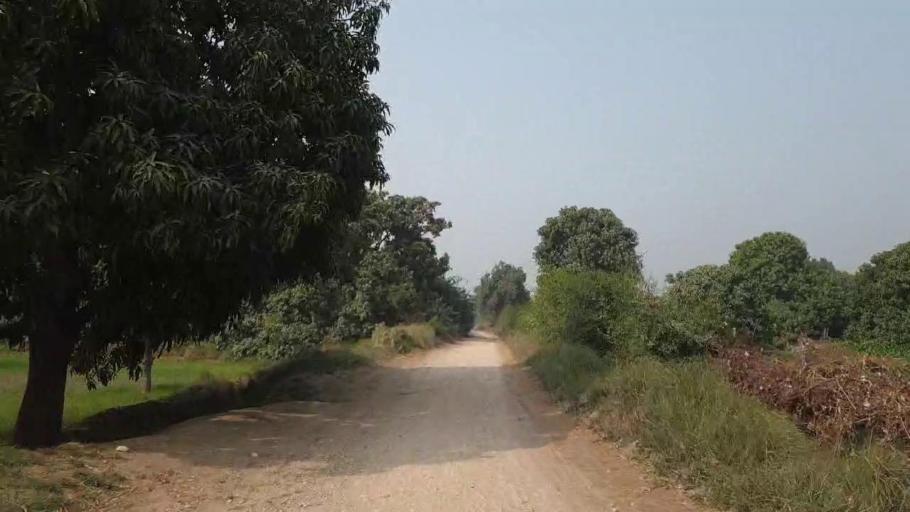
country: PK
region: Sindh
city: Tando Muhammad Khan
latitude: 25.2055
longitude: 68.5615
